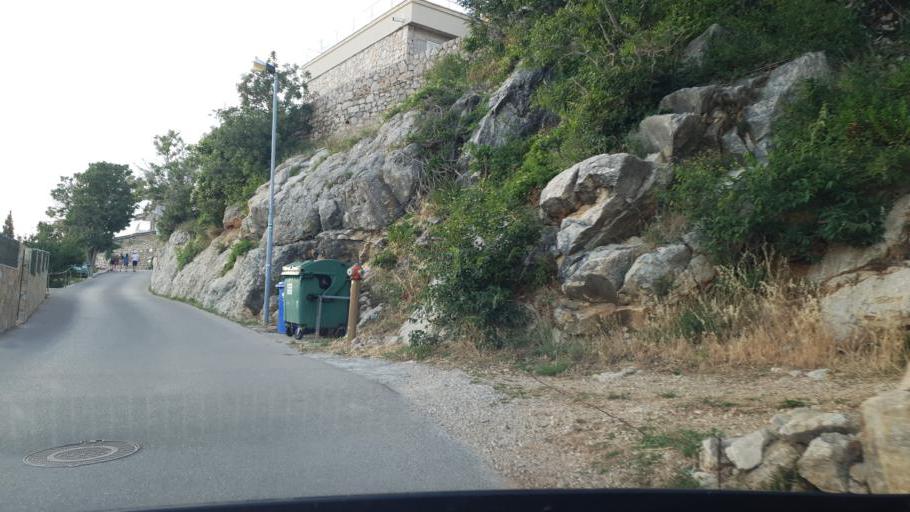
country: HR
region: Primorsko-Goranska
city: Punat
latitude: 44.9568
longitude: 14.6899
